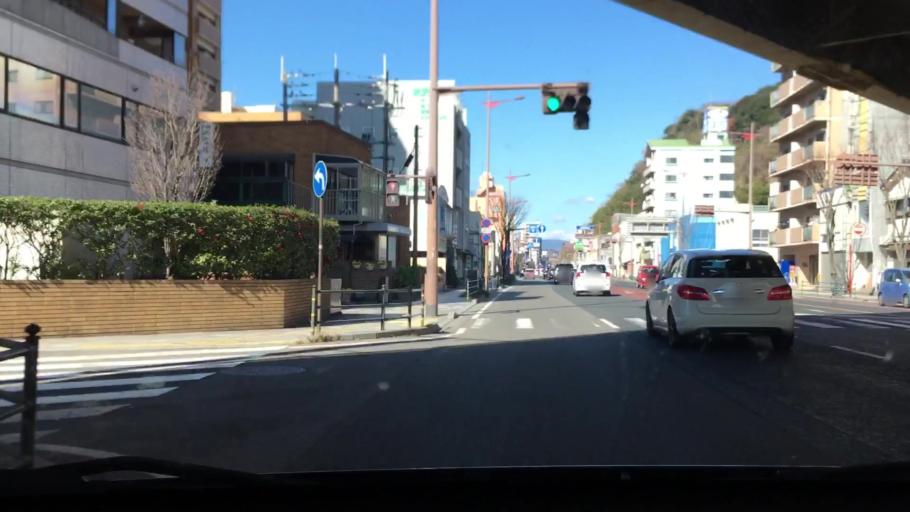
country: JP
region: Kagoshima
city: Kagoshima-shi
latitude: 31.5932
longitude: 130.5439
